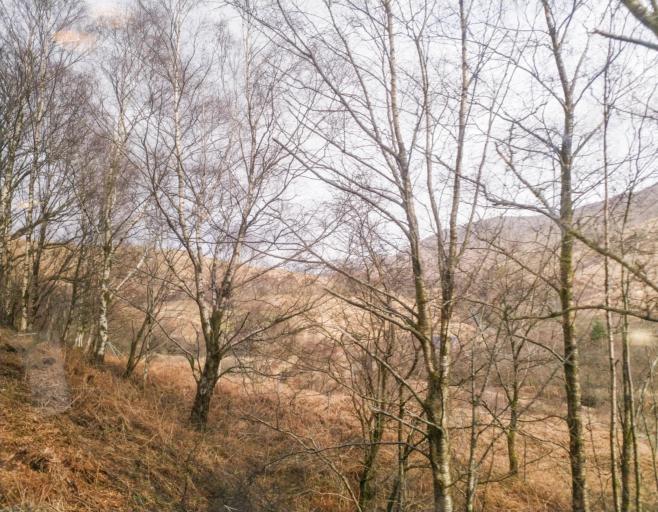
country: GB
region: Scotland
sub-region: Argyll and Bute
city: Garelochhead
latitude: 56.3492
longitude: -4.7037
